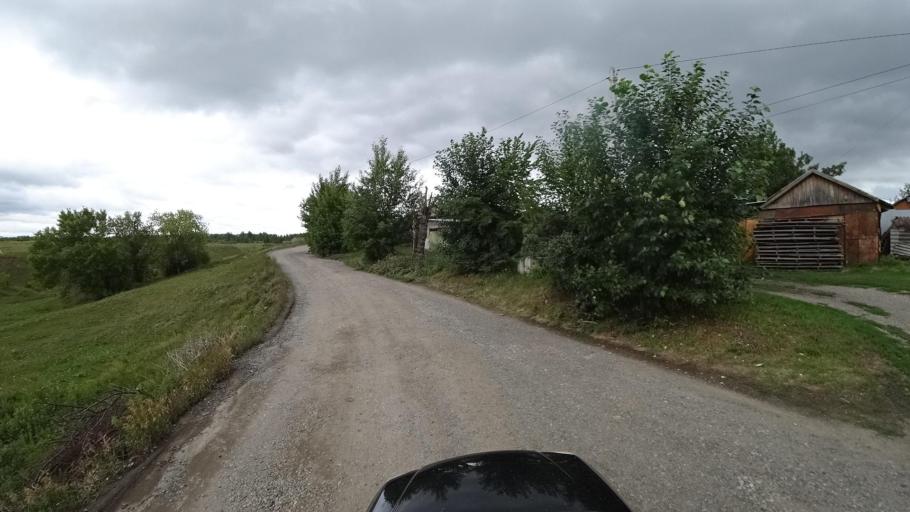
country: RU
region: Sverdlovsk
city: Kamyshlov
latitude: 56.8504
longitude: 62.6829
